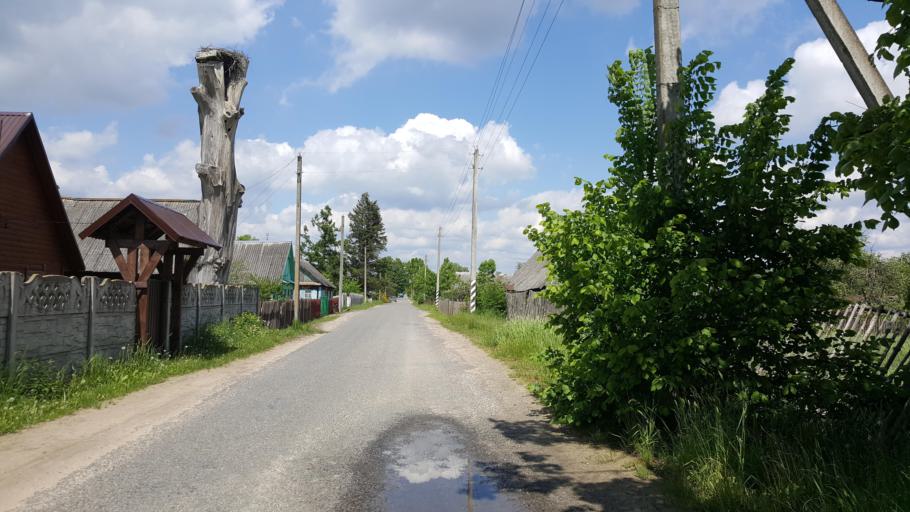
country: BY
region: Brest
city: Kamyanyets
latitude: 52.4479
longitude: 23.9743
